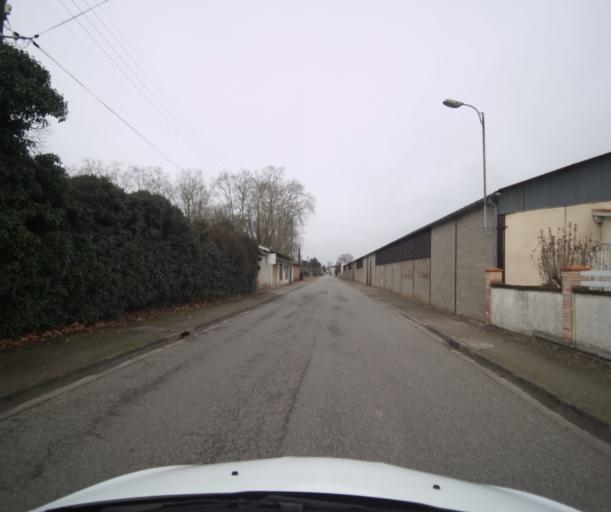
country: FR
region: Midi-Pyrenees
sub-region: Departement du Tarn-et-Garonne
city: Castelsarrasin
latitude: 44.0478
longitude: 1.1123
